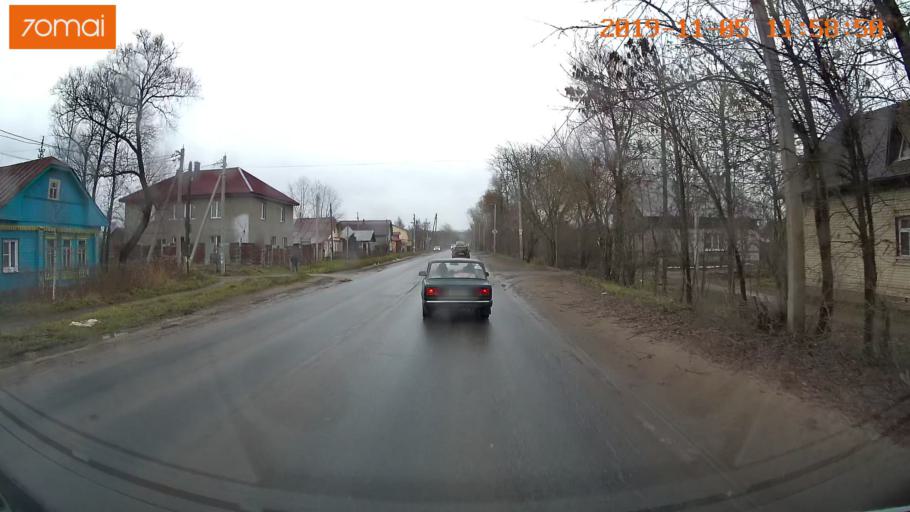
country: RU
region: Ivanovo
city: Kokhma
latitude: 56.9801
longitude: 41.0427
